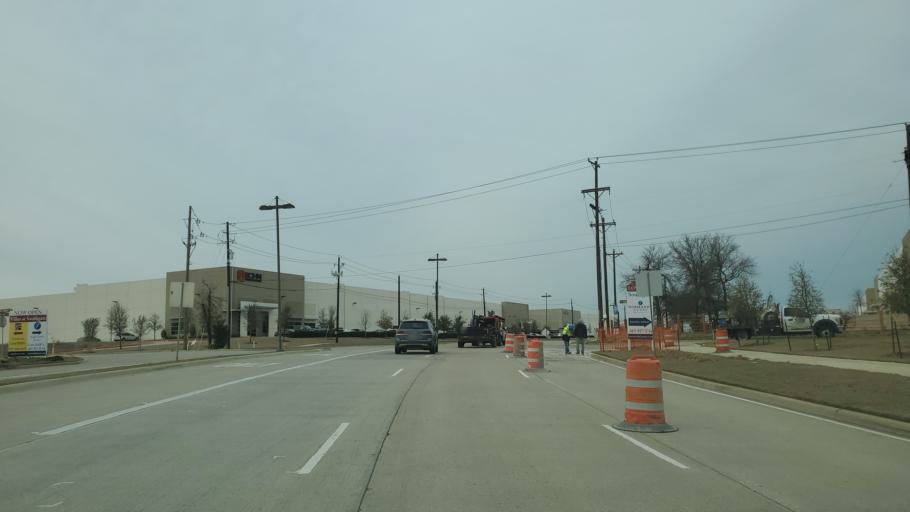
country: US
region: Texas
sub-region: Dallas County
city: Coppell
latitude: 32.9896
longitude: -97.0452
